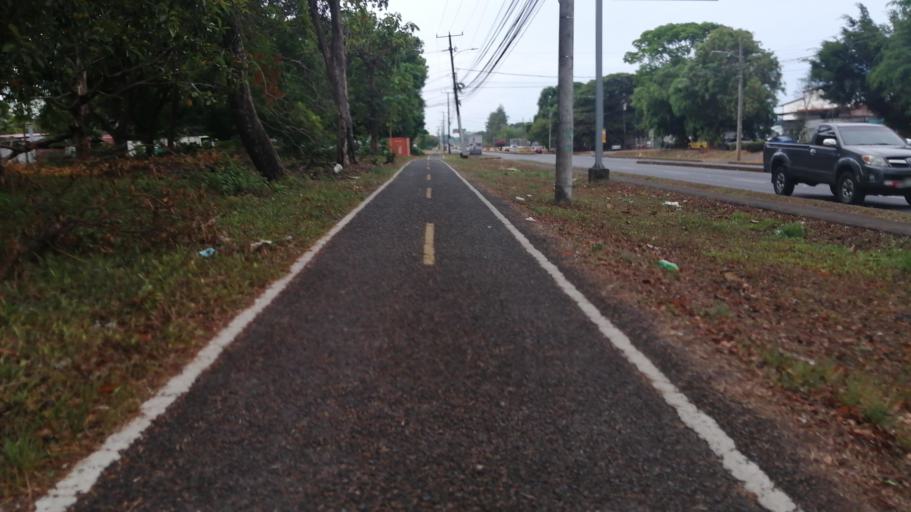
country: PA
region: Chiriqui
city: David
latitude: 8.4088
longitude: -82.4305
